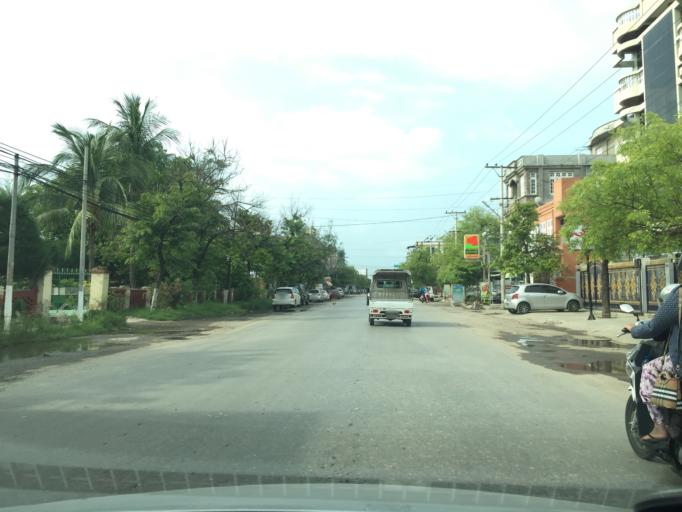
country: MM
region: Mandalay
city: Mandalay
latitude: 21.9724
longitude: 96.0805
